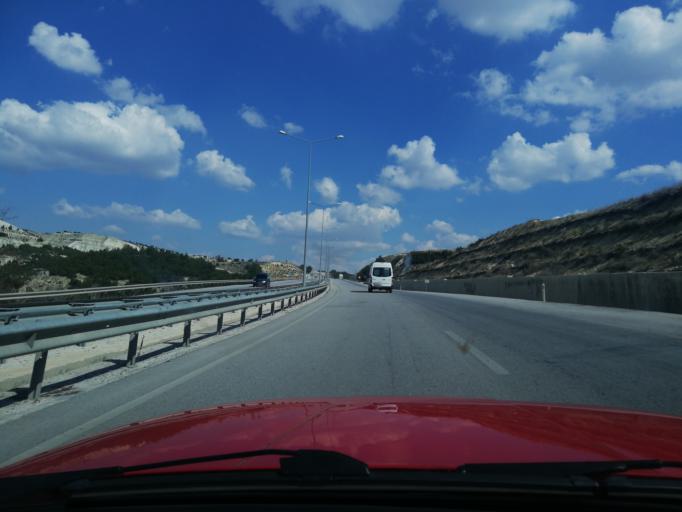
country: TR
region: Burdur
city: Burdur
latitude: 37.7011
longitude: 30.3103
